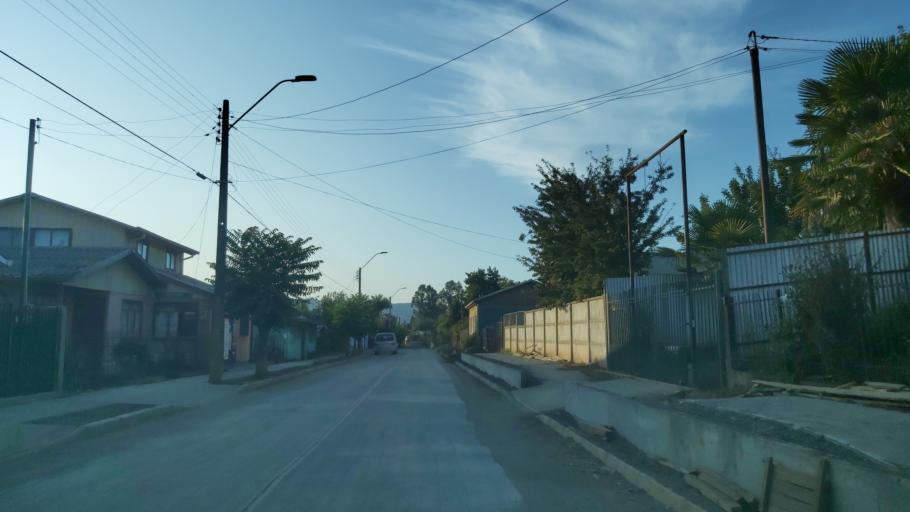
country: CL
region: Biobio
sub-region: Provincia de Biobio
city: La Laja
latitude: -37.1619
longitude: -72.9100
